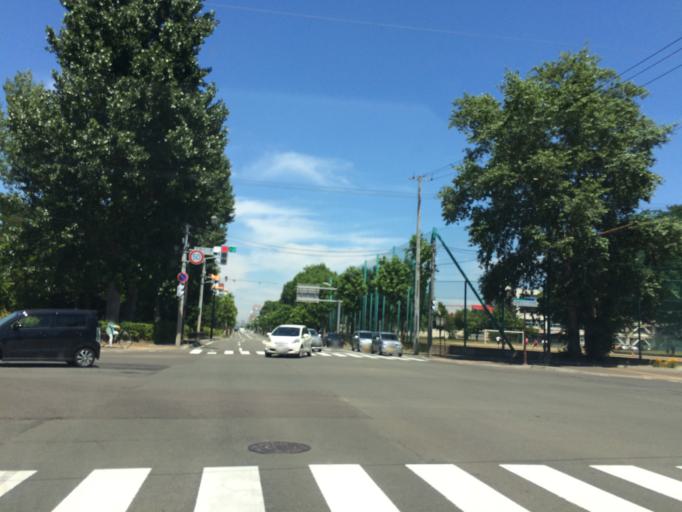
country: JP
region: Hokkaido
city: Sapporo
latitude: 42.9978
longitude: 141.3489
